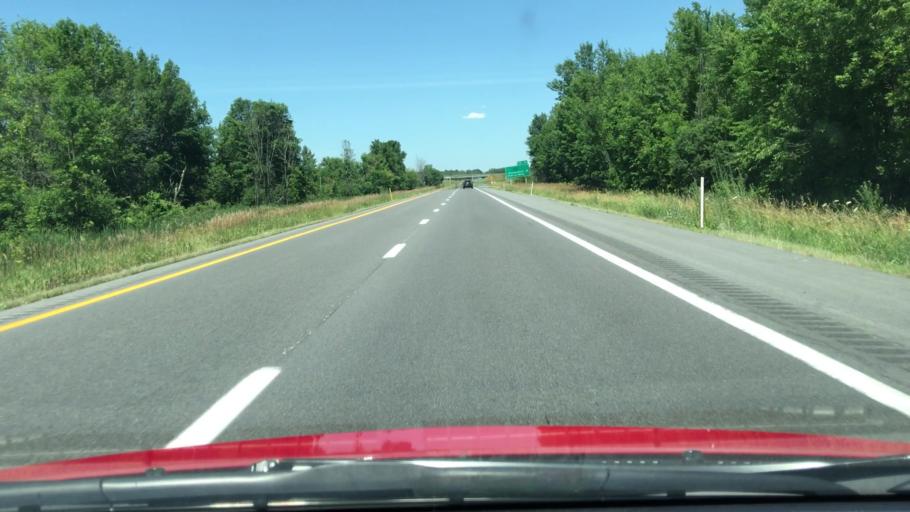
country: US
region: New York
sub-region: Clinton County
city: Cumberland Head
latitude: 44.7753
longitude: -73.4351
